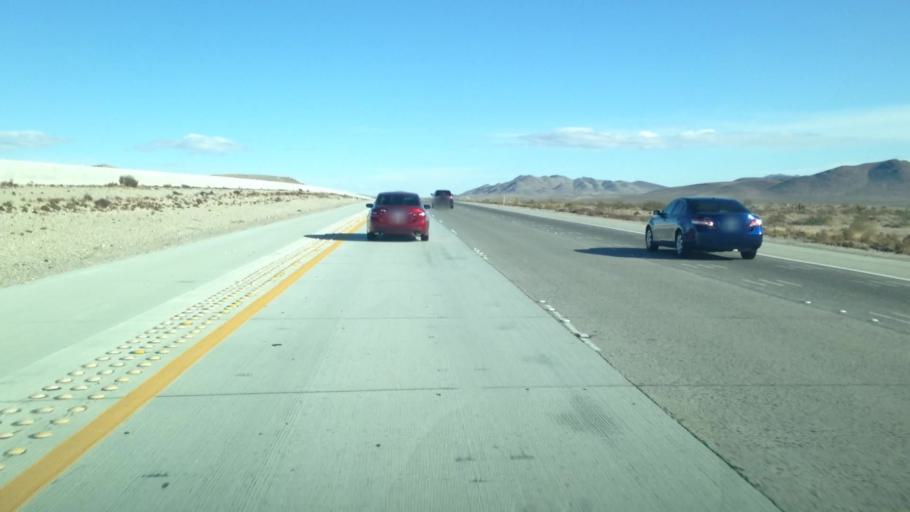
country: US
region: Nevada
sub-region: Clark County
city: Enterprise
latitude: 35.8389
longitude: -115.2797
